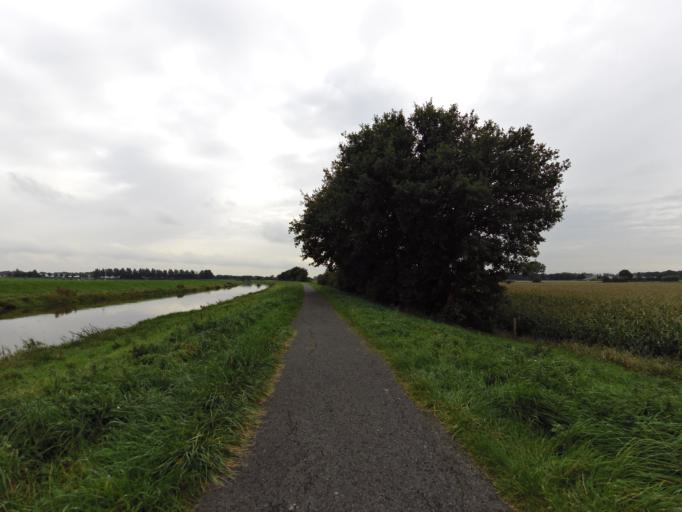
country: DE
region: North Rhine-Westphalia
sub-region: Regierungsbezirk Munster
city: Isselburg
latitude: 51.8595
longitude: 6.4568
